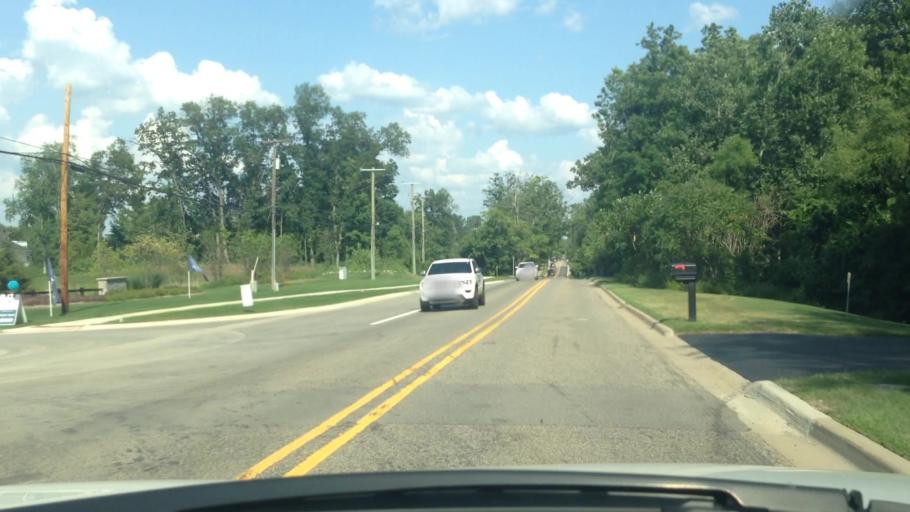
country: US
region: Michigan
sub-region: Oakland County
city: Clarkston
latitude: 42.7340
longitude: -83.3662
